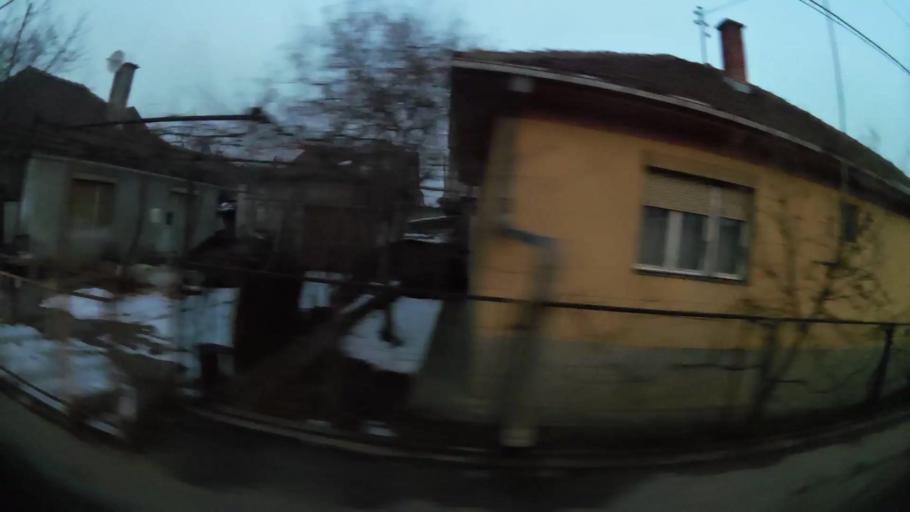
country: MK
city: Creshevo
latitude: 42.0083
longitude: 21.5118
